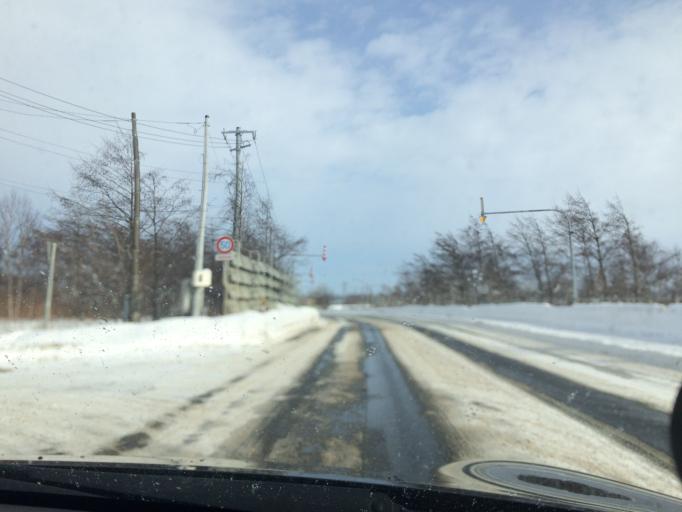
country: JP
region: Hokkaido
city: Kitahiroshima
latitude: 43.0187
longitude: 141.5798
